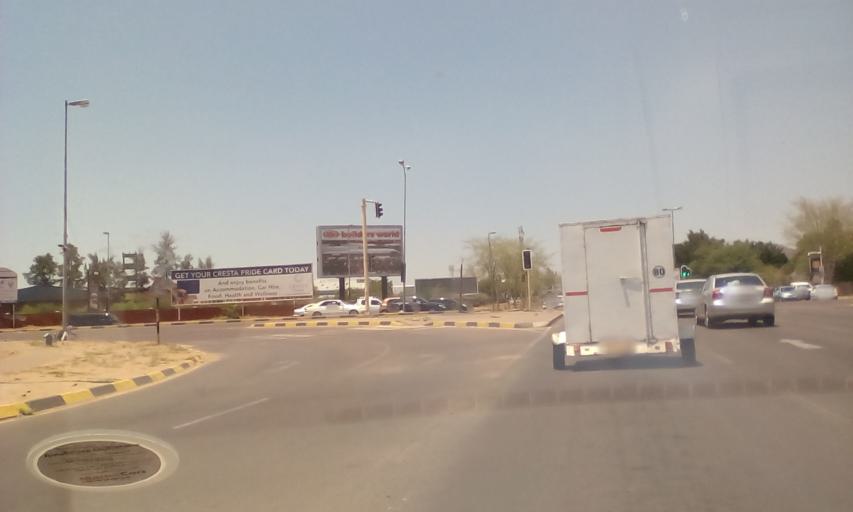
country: BW
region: South East
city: Gaborone
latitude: -24.6550
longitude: 25.9005
